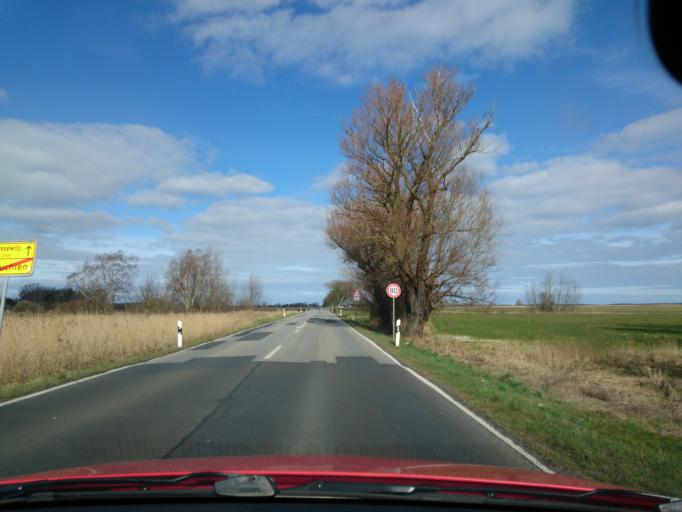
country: DE
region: Mecklenburg-Vorpommern
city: Barth
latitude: 54.3839
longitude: 12.6777
